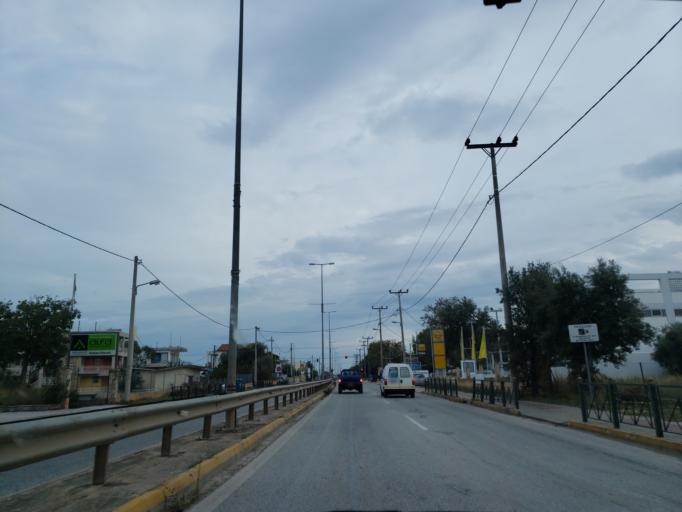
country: GR
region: Attica
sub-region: Nomarchia Anatolikis Attikis
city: Nea Makri
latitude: 38.0974
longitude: 23.9720
